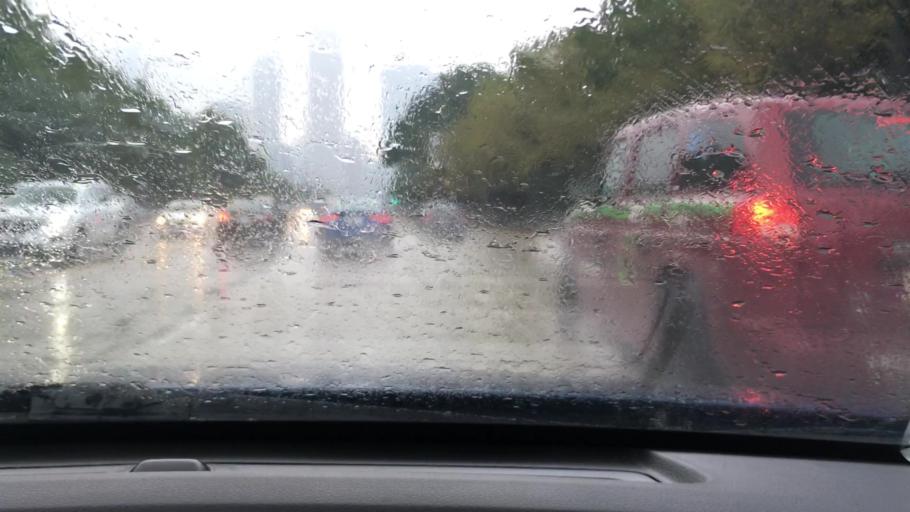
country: US
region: Illinois
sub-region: Cook County
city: Chicago
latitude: 41.8712
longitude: -87.6205
